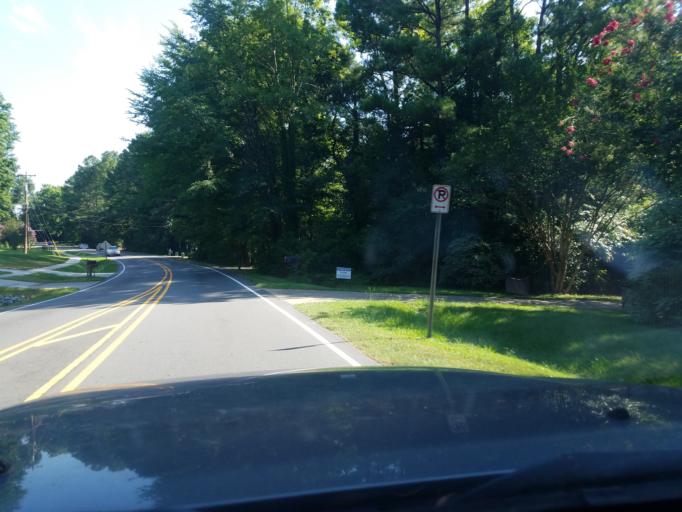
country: US
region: North Carolina
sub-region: Durham County
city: Durham
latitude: 35.9290
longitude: -78.9602
